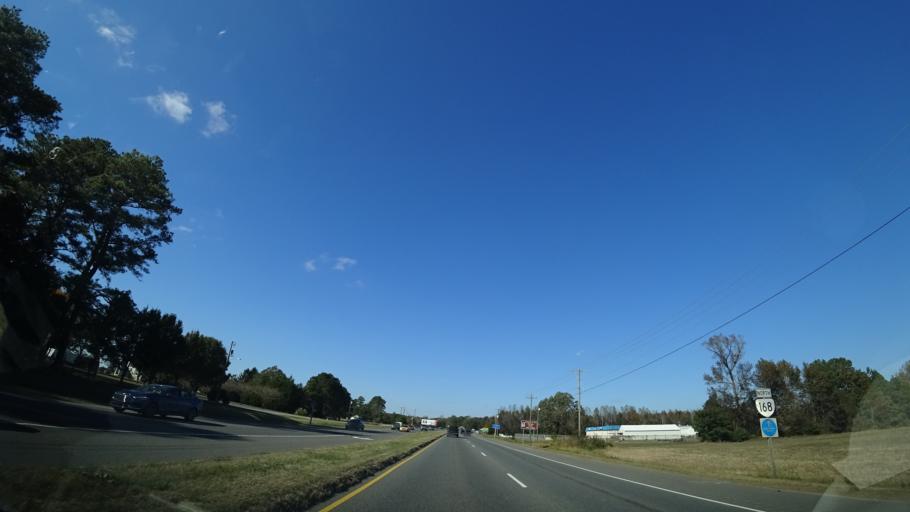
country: US
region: North Carolina
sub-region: Currituck County
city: Moyock
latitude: 36.5535
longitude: -76.1947
